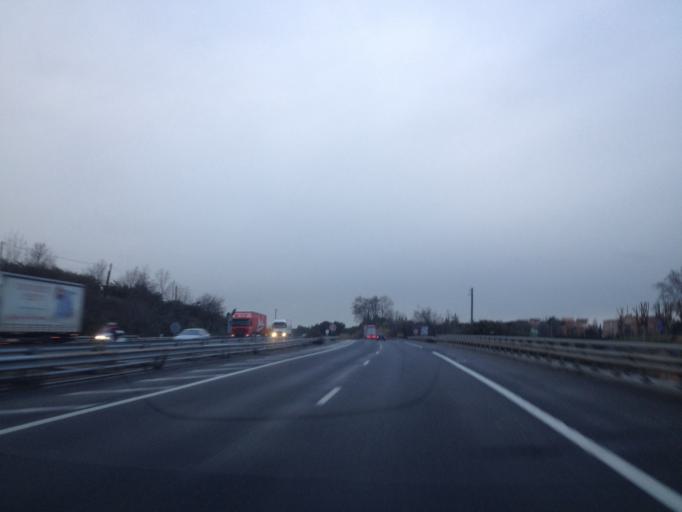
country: FR
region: Provence-Alpes-Cote d'Azur
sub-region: Departement des Bouches-du-Rhone
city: Aix-en-Provence
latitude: 43.5190
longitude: 5.4275
